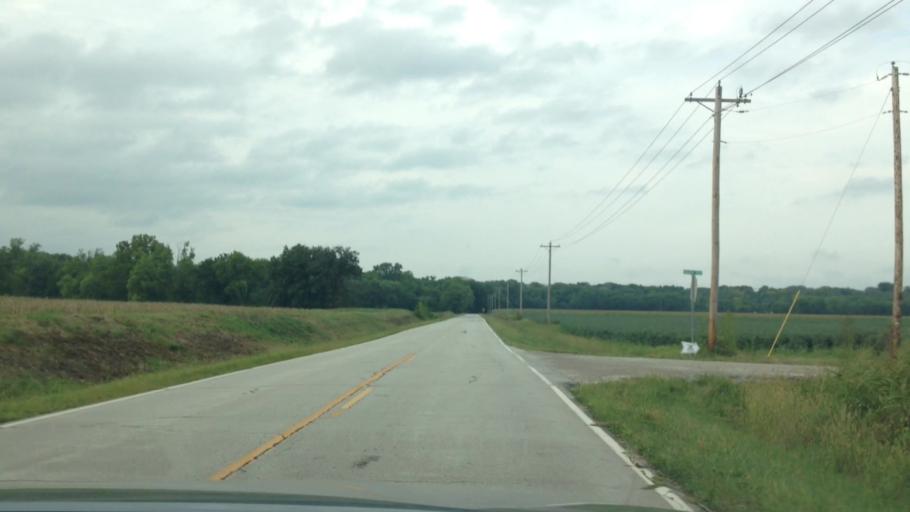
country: US
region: Missouri
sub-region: Clay County
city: Smithville
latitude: 39.3975
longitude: -94.6620
